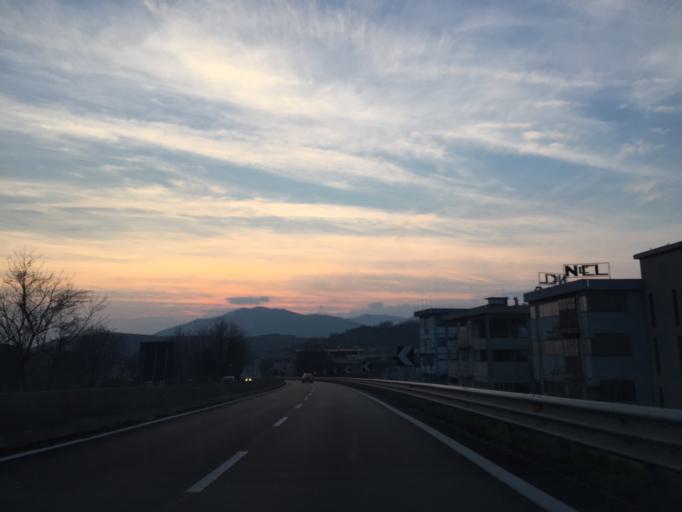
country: IT
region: Campania
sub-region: Provincia di Avellino
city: Solofra
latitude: 40.8340
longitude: 14.8281
